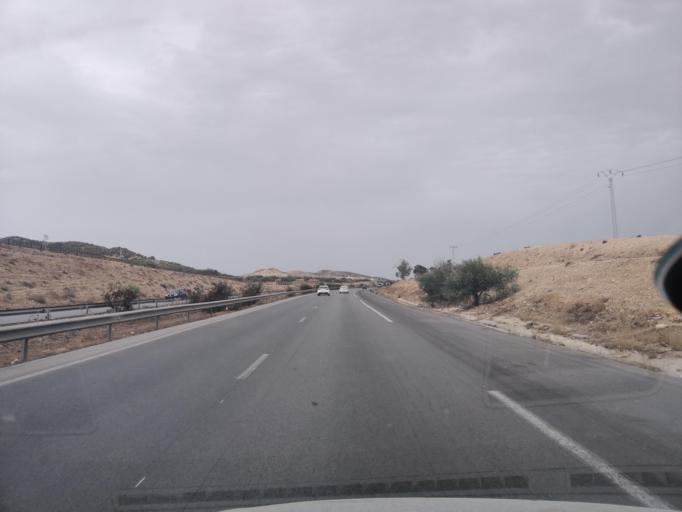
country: TN
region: Susah
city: Harqalah
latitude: 36.2272
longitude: 10.4144
